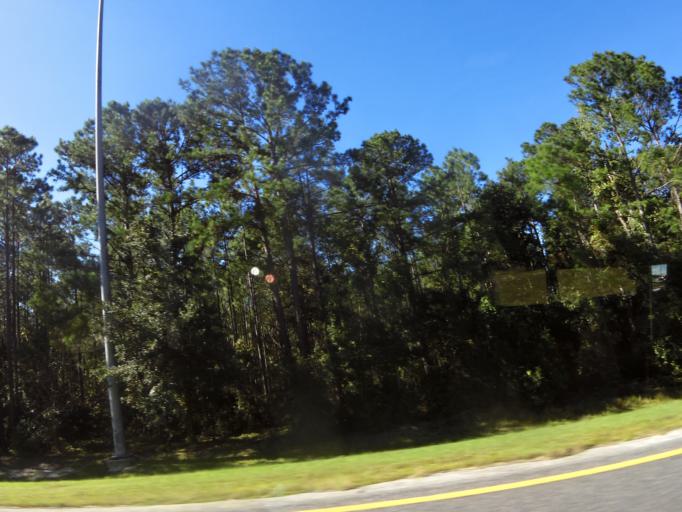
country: US
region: Florida
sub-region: Saint Johns County
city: Palm Valley
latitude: 30.1028
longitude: -81.4640
